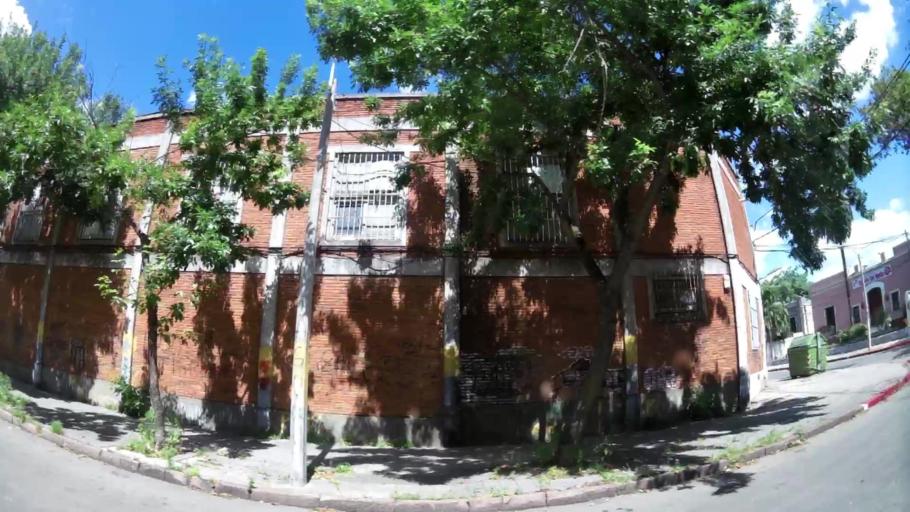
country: UY
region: Montevideo
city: Montevideo
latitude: -34.8778
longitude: -56.1931
